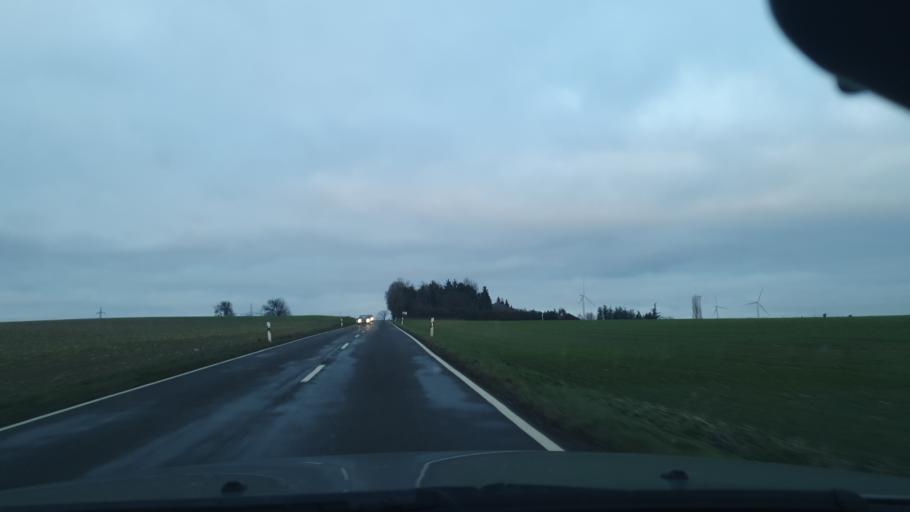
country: DE
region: Rheinland-Pfalz
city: Rosenkopf
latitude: 49.3418
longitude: 7.4295
